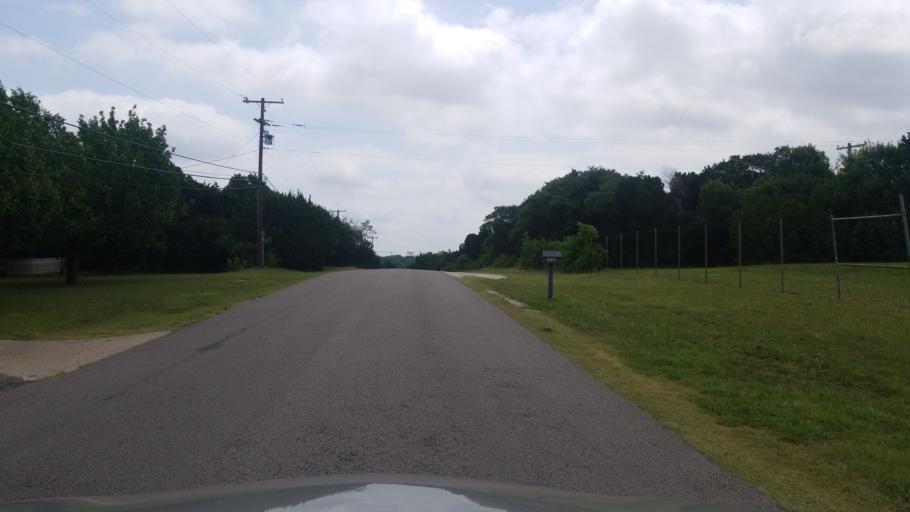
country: US
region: Texas
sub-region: Dallas County
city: Duncanville
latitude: 32.6765
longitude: -96.9307
